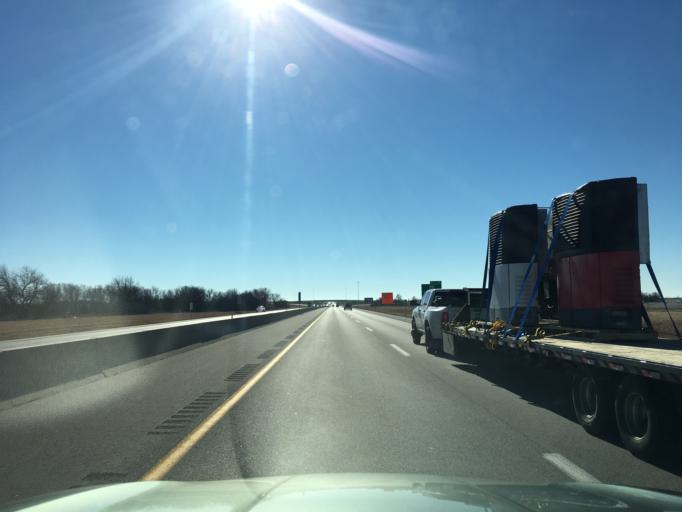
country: US
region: Kansas
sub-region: Sumner County
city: Wellington
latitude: 37.2889
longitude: -97.3403
